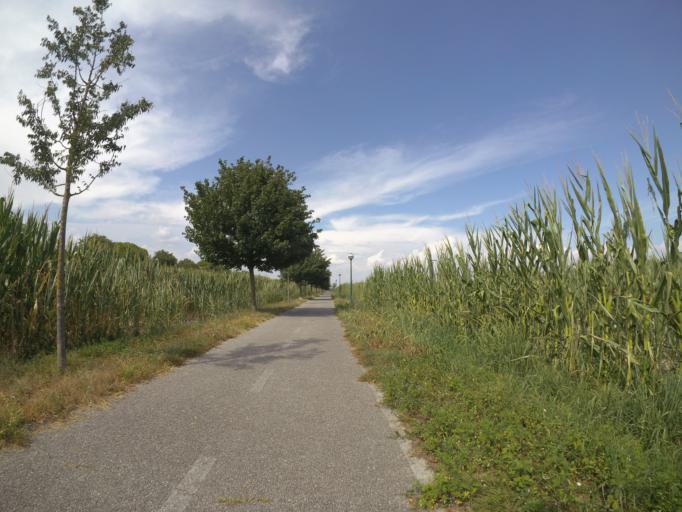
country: IT
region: Veneto
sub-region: Provincia di Venezia
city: Bibione
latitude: 45.6674
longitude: 13.0698
